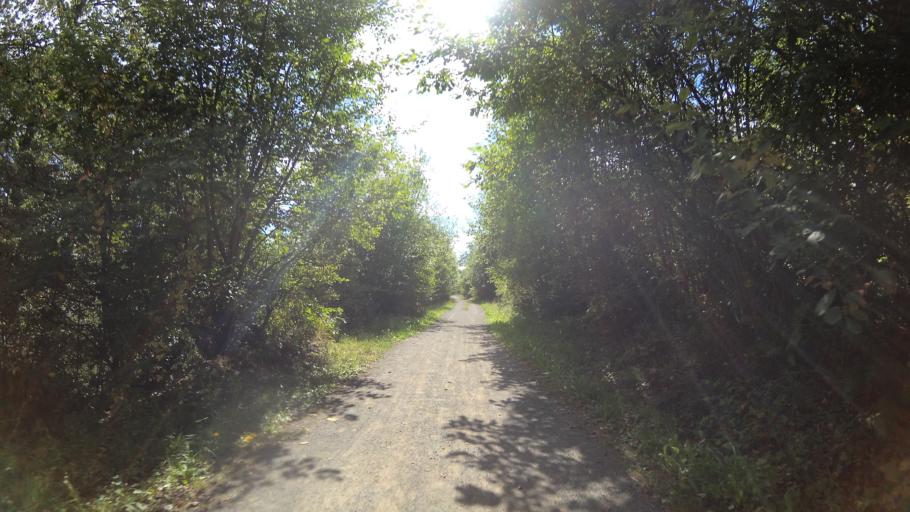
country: DE
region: Saarland
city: Freisen
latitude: 49.5198
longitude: 7.2361
